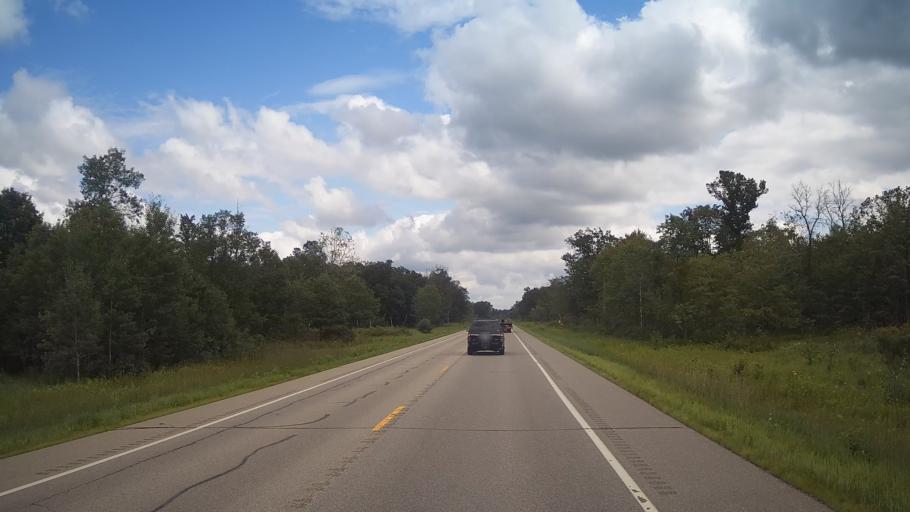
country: US
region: Wisconsin
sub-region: Adams County
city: Friendship
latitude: 44.0256
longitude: -89.7027
